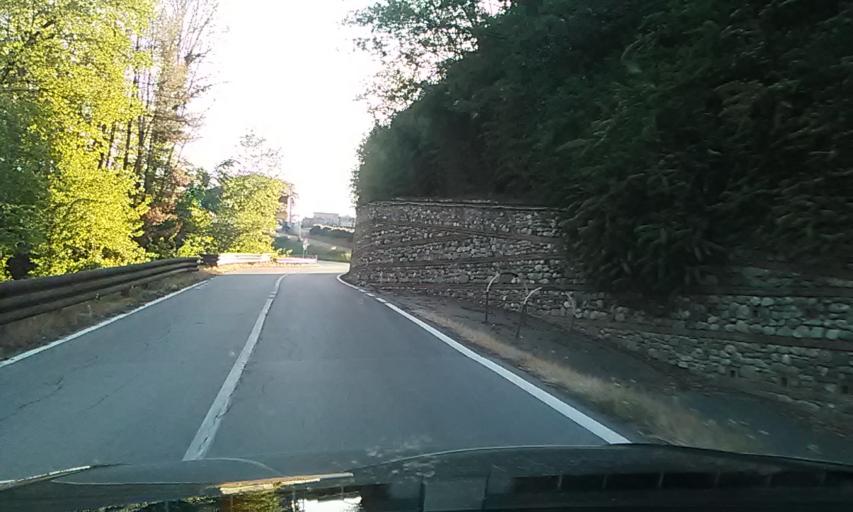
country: IT
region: Piedmont
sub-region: Provincia di Novara
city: Barengo
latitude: 45.5724
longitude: 8.5090
